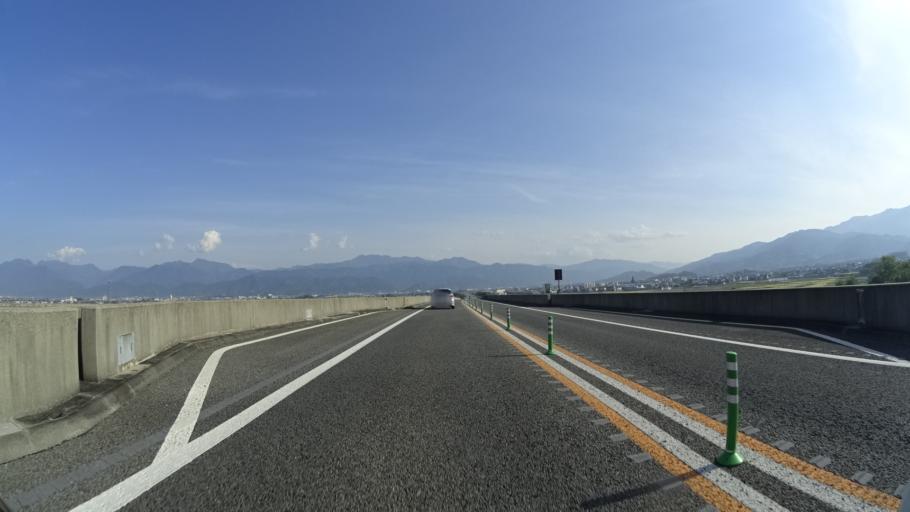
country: JP
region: Ehime
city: Saijo
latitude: 33.9497
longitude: 133.0693
